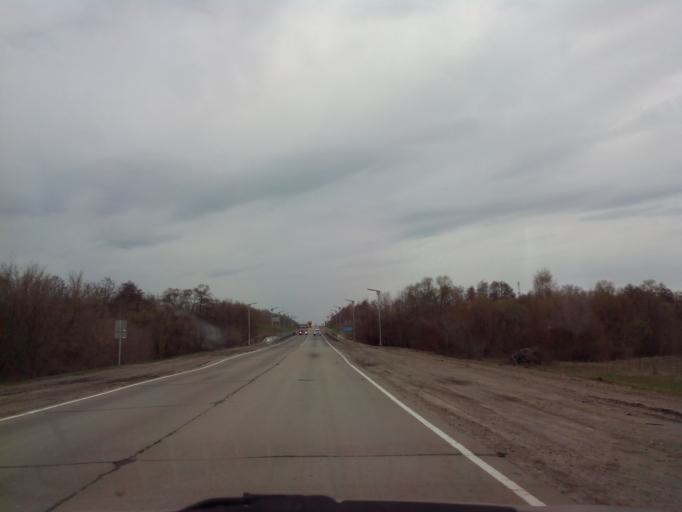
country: RU
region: Tambov
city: Znamenka
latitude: 52.3947
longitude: 41.3986
